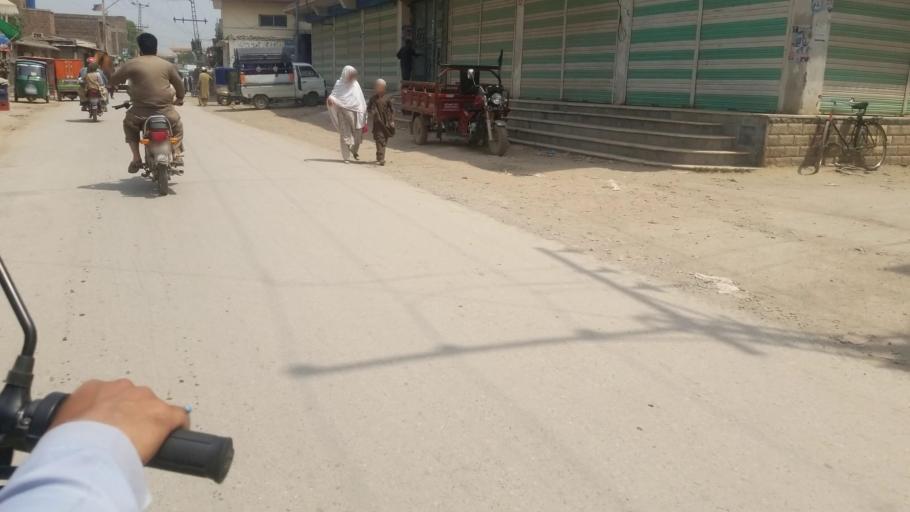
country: PK
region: Khyber Pakhtunkhwa
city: Peshawar
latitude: 34.0257
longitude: 71.6222
